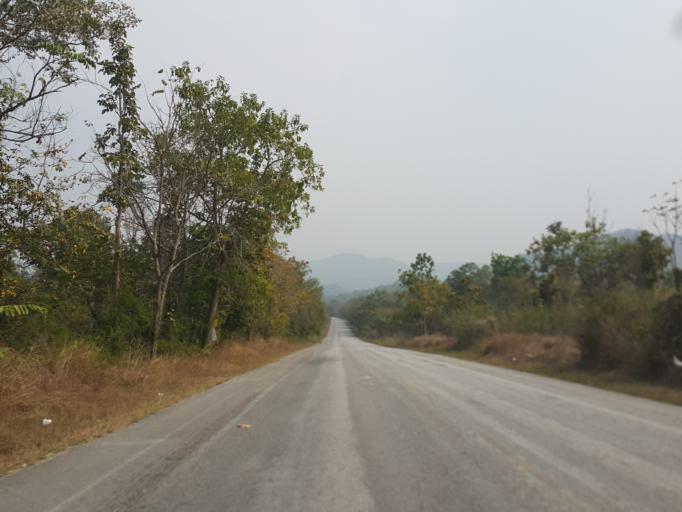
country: TH
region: Lampang
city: Thoen
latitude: 17.6303
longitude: 99.2621
